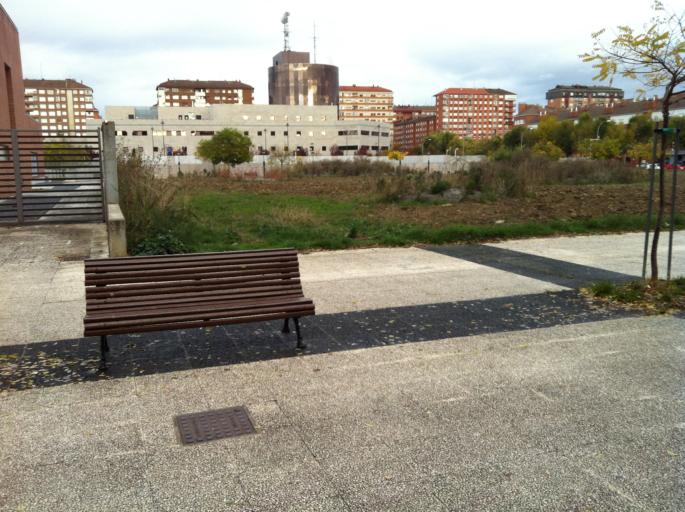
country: ES
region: Basque Country
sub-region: Provincia de Alava
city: Gasteiz / Vitoria
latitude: 42.8635
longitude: -2.6882
